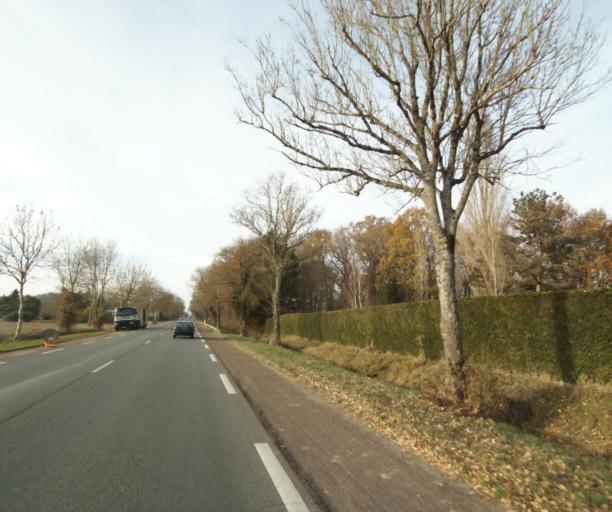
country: FR
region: Poitou-Charentes
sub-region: Departement de la Charente-Maritime
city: Saint-Georges-des-Coteaux
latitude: 45.7746
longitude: -0.6944
